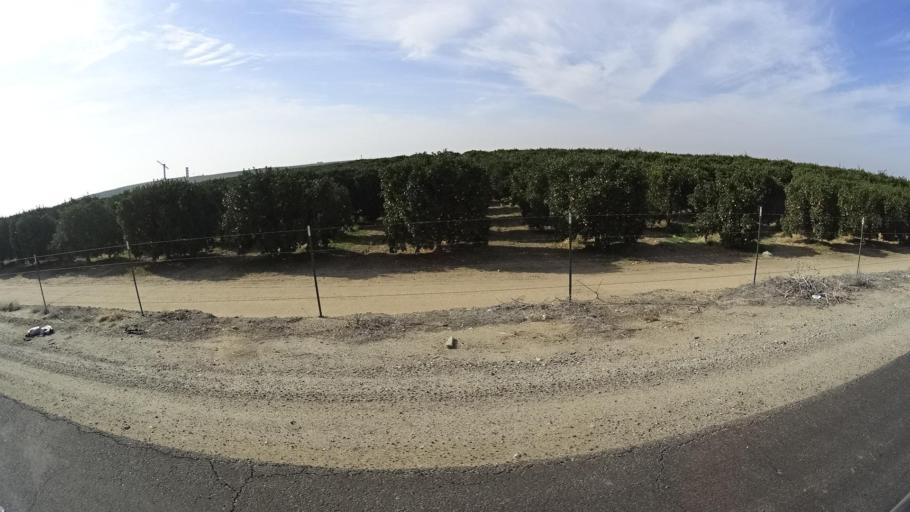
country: US
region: California
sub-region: Kern County
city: Lamont
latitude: 35.3562
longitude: -118.8432
